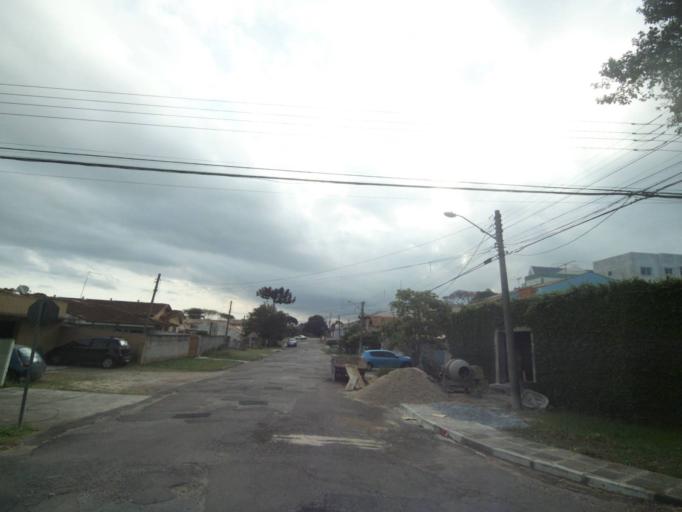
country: BR
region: Parana
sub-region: Pinhais
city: Pinhais
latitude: -25.4160
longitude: -49.2138
